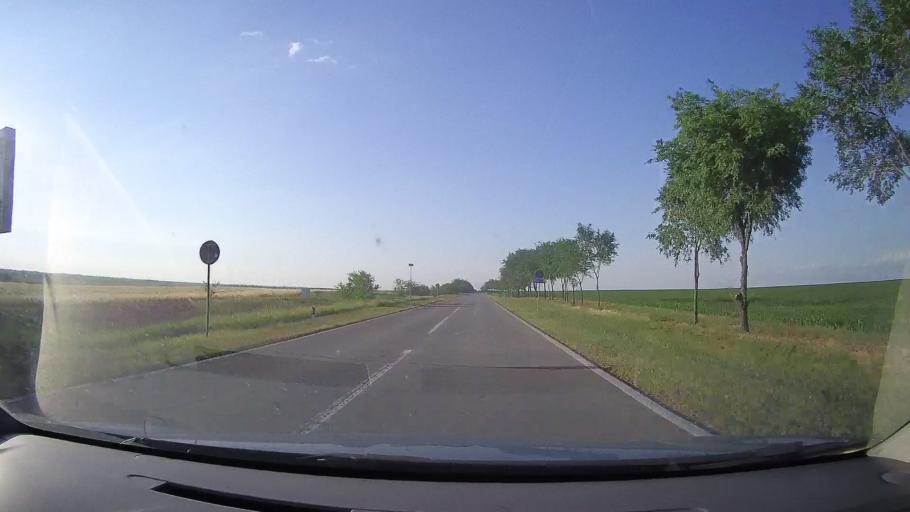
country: RO
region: Timis
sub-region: Comuna Moravita
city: Moravita
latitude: 45.1987
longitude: 21.3000
